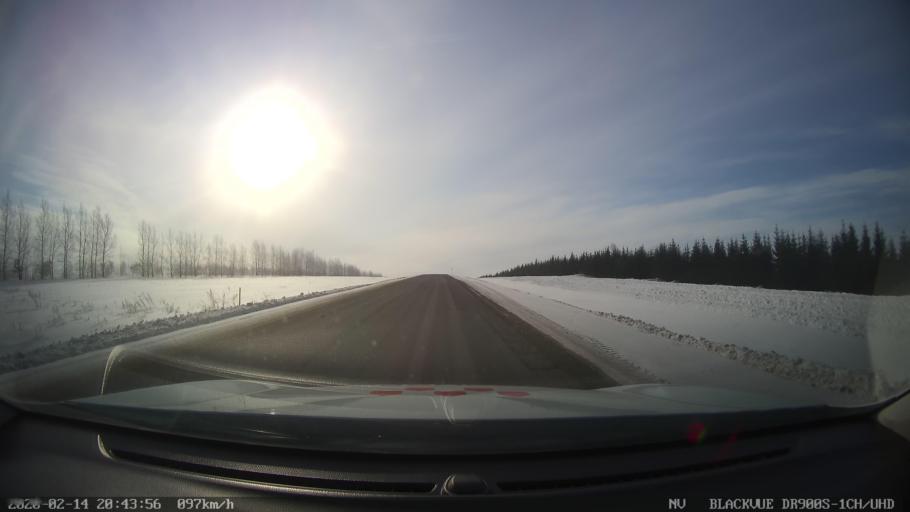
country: RU
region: Tatarstan
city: Kuybyshevskiy Zaton
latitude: 55.3013
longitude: 49.1476
